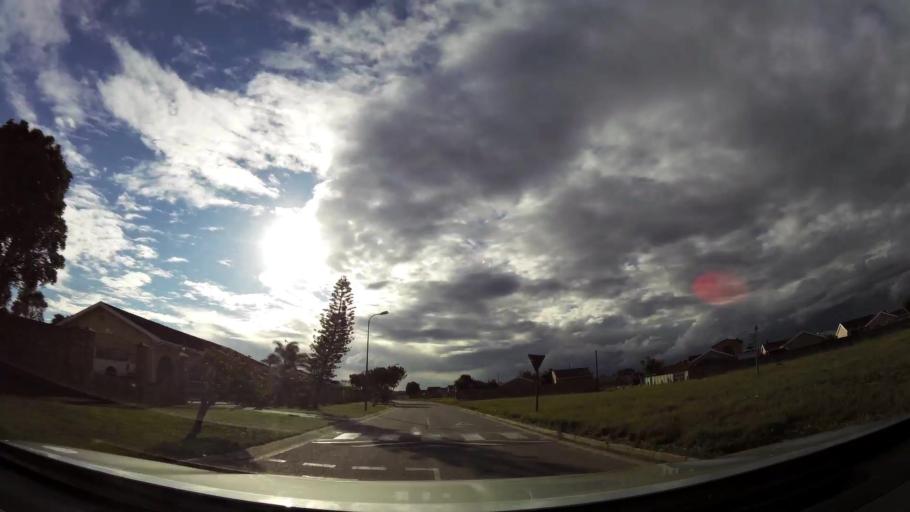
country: ZA
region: Eastern Cape
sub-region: Nelson Mandela Bay Metropolitan Municipality
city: Port Elizabeth
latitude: -33.9534
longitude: 25.4834
